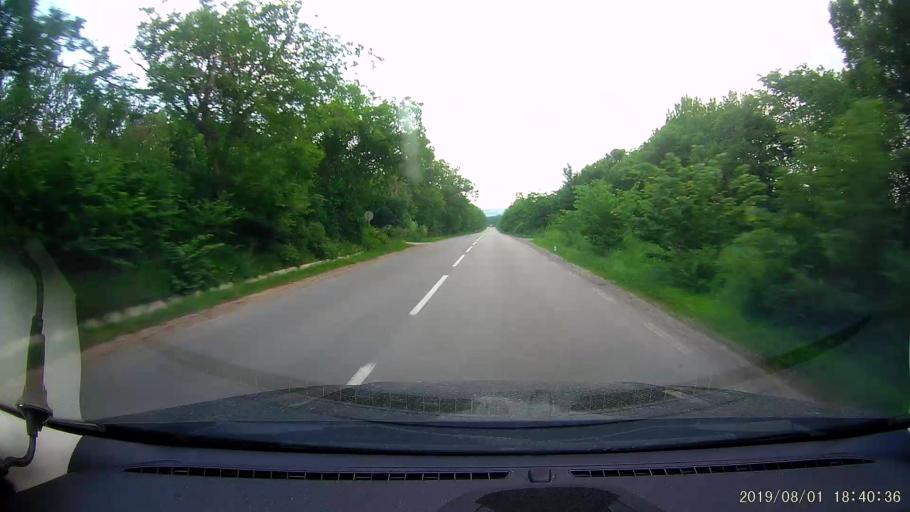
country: BG
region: Shumen
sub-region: Obshtina Khitrino
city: Gara Khitrino
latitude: 43.3633
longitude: 26.9200
